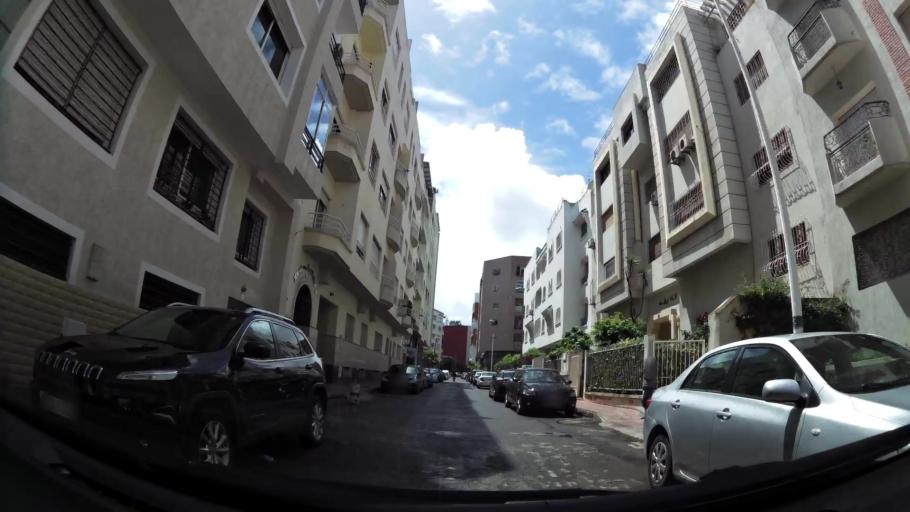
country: MA
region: Grand Casablanca
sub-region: Casablanca
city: Casablanca
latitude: 33.5750
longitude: -7.6378
